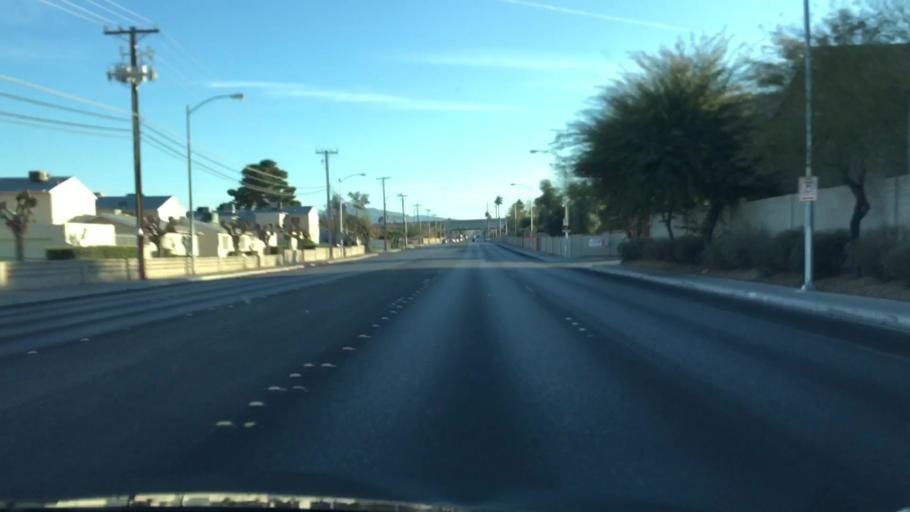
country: US
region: Nevada
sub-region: Clark County
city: Whitney
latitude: 36.0976
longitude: -115.0733
